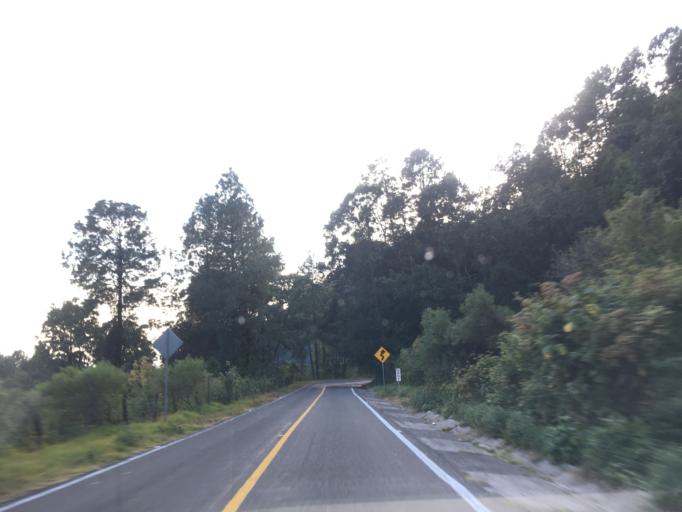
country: MX
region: Michoacan
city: Tzitzio
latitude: 19.6711
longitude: -100.9193
